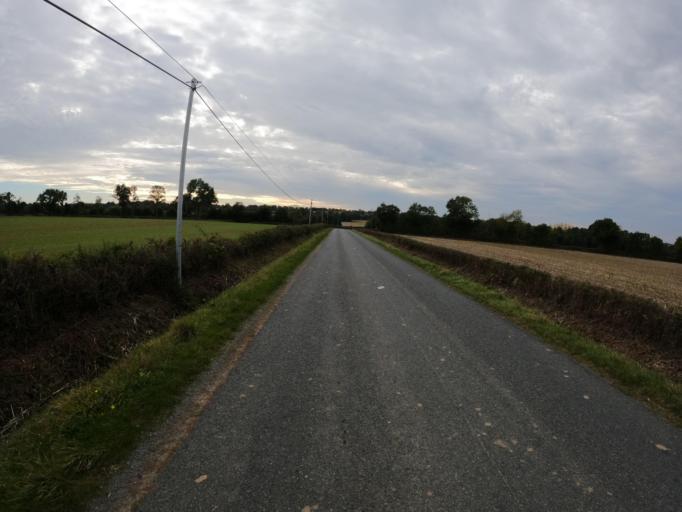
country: FR
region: Pays de la Loire
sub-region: Departement de Maine-et-Loire
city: Saint-Christophe-du-Bois
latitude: 47.0259
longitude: -0.9619
